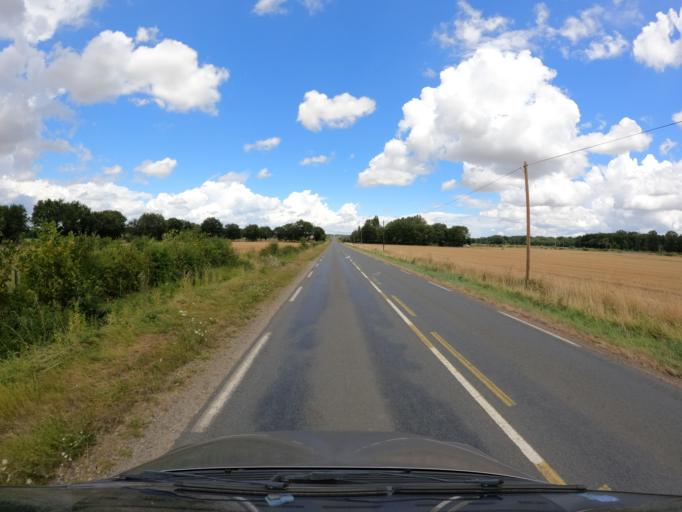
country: FR
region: Pays de la Loire
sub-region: Departement de la Sarthe
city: Solesmes
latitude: 47.8653
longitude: -0.3138
